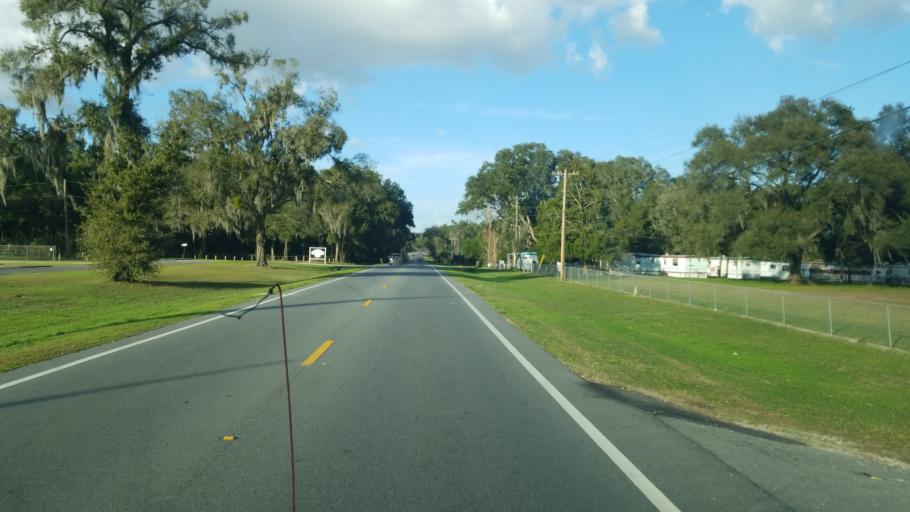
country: US
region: Florida
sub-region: Marion County
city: Ocala
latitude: 29.2536
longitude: -82.1153
